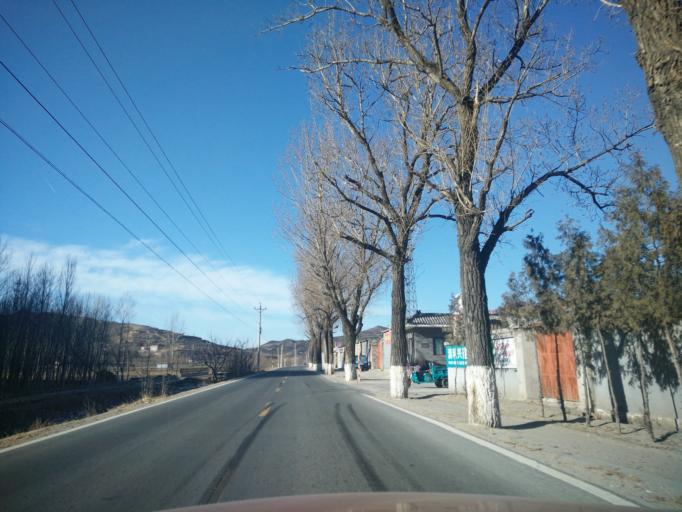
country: CN
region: Beijing
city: Yanchi
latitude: 39.9944
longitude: 115.7666
